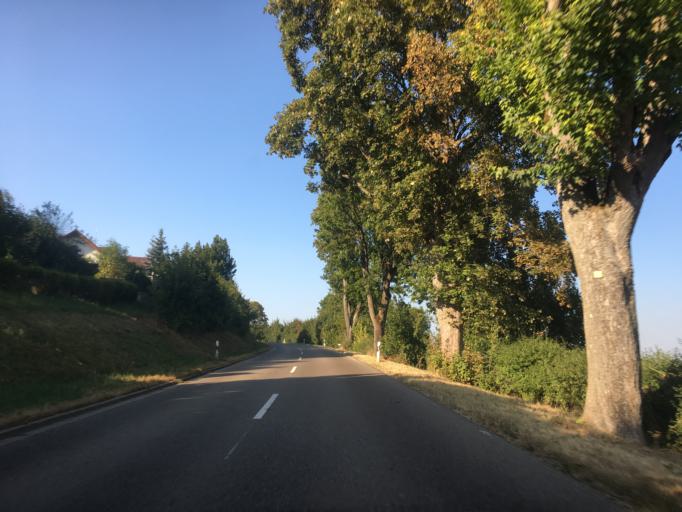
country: DE
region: Baden-Wuerttemberg
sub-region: Tuebingen Region
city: Hayingen
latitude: 48.2782
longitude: 9.4737
